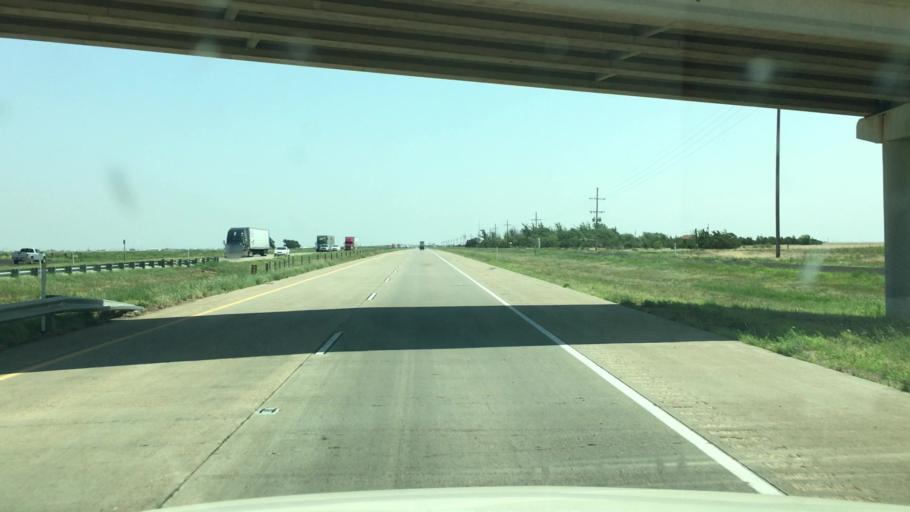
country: US
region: Texas
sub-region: Potter County
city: Bushland
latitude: 35.2043
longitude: -102.1498
